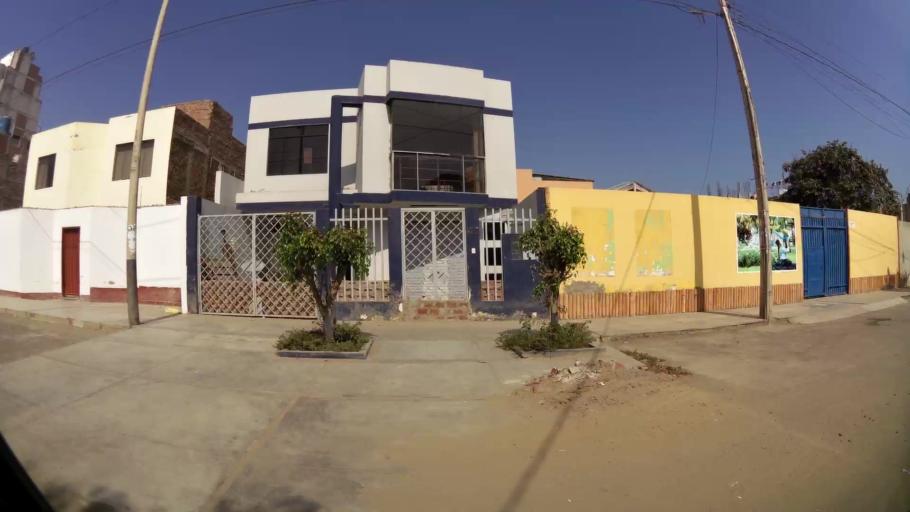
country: PE
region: La Libertad
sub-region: Provincia de Trujillo
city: Buenos Aires
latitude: -8.1234
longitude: -79.0437
